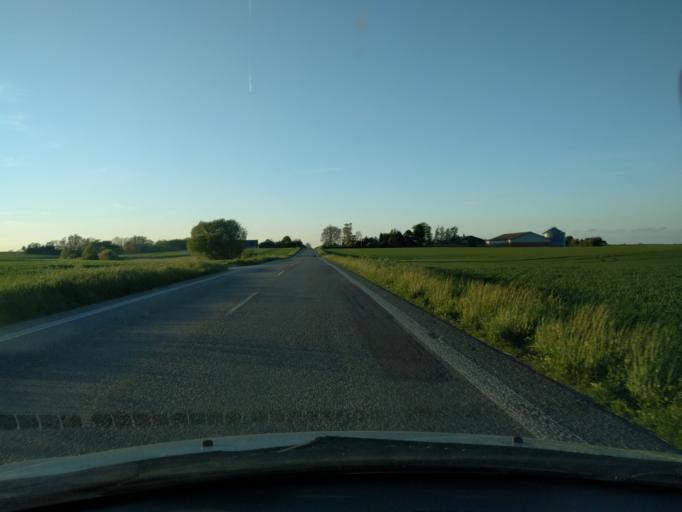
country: DK
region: Zealand
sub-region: Guldborgsund Kommune
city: Stubbekobing
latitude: 54.8267
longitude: 11.9949
